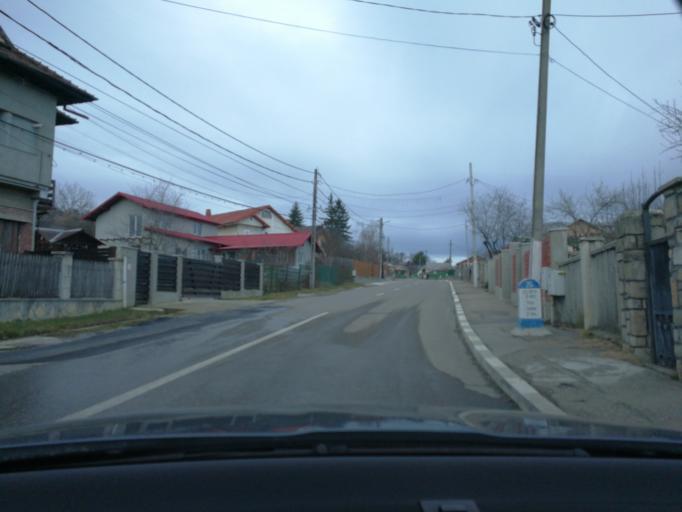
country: RO
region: Prahova
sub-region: Municipiul Campina
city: Campina
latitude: 45.1277
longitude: 25.7095
